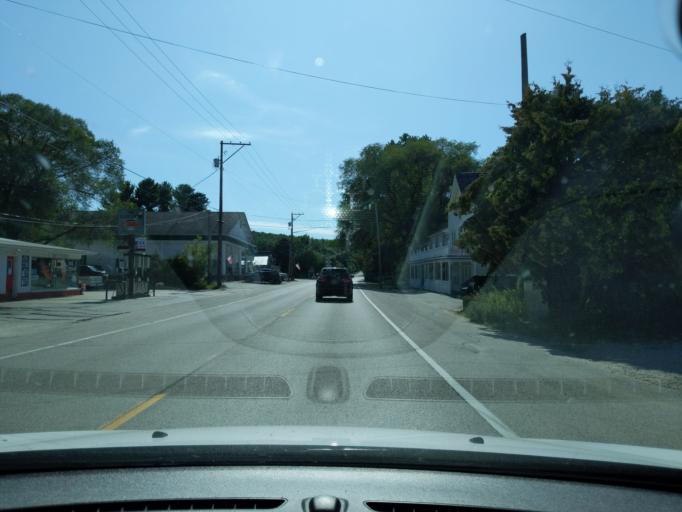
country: US
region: Michigan
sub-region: Delta County
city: Escanaba
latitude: 45.2537
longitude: -87.0737
